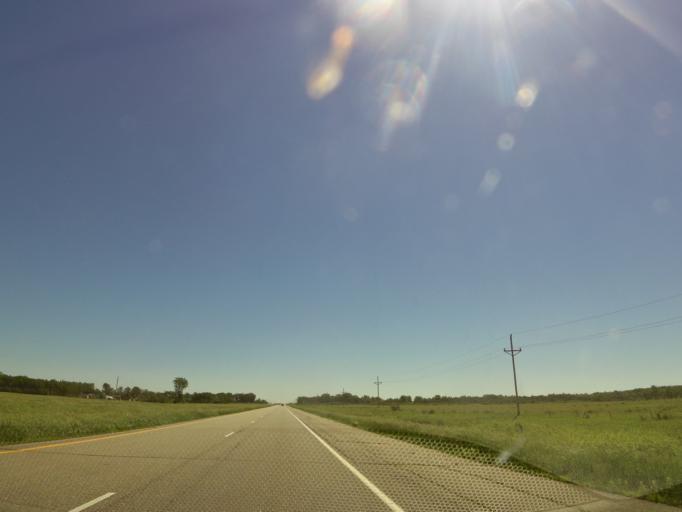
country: US
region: Minnesota
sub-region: Polk County
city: Crookston
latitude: 47.7605
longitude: -96.4260
